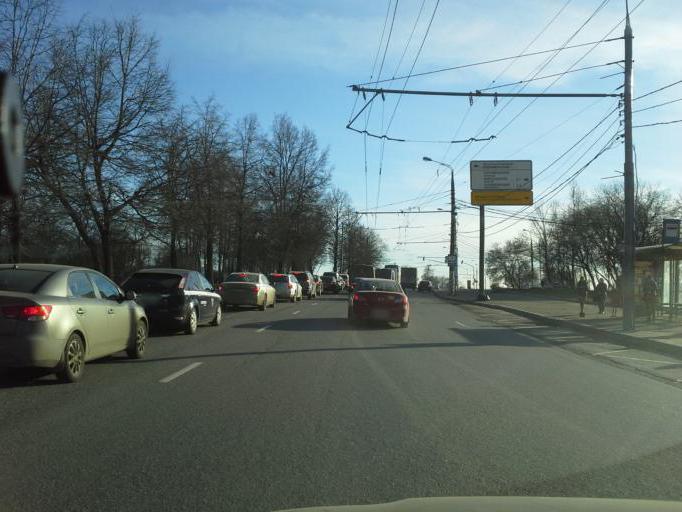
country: RU
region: Moscow
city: Kolomenskoye
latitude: 55.6694
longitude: 37.6614
